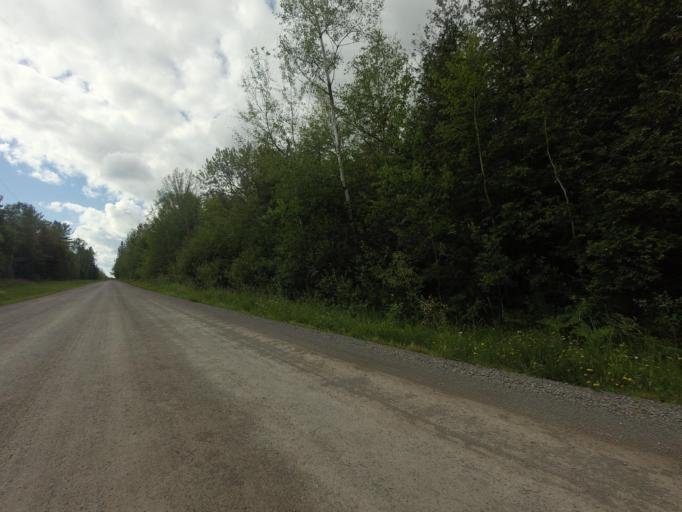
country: CA
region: Ontario
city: Carleton Place
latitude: 45.3113
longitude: -76.1338
